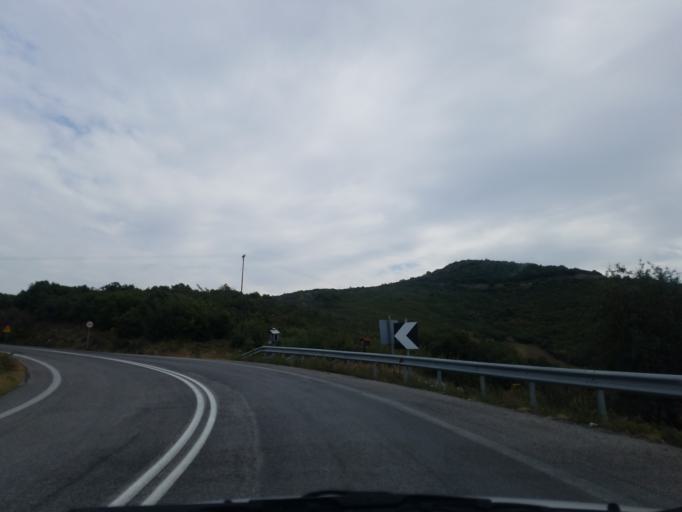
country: GR
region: Central Greece
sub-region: Nomos Fthiotidos
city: Domokos
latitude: 39.1447
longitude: 22.3042
